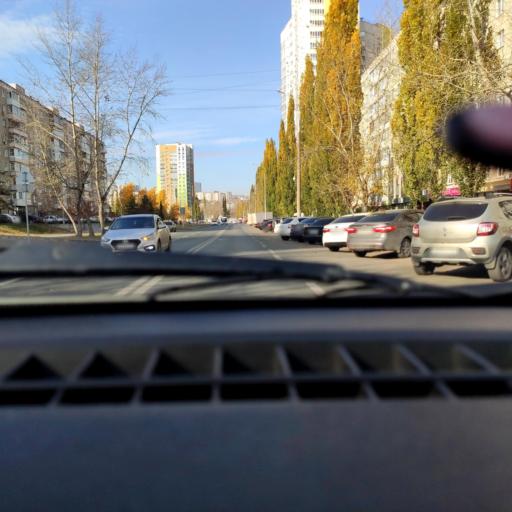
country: RU
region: Bashkortostan
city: Ufa
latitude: 54.7673
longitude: 56.0607
